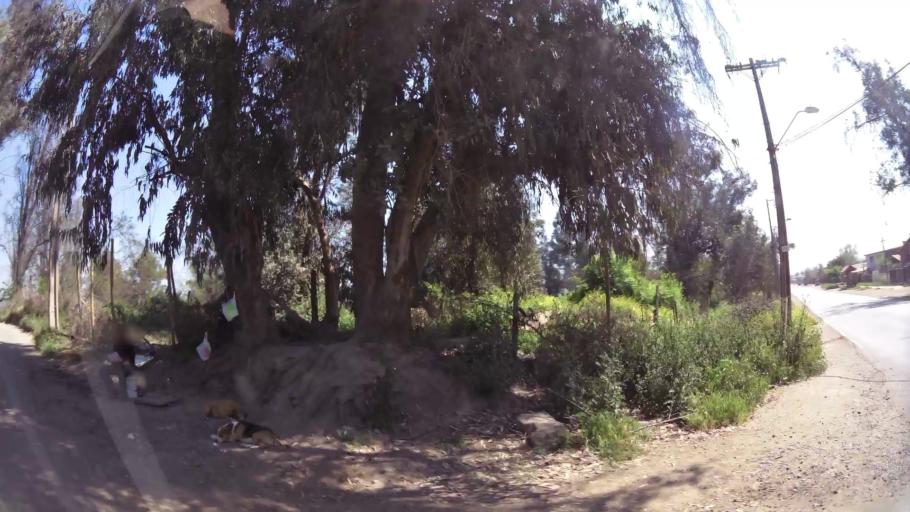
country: CL
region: Santiago Metropolitan
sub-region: Provincia de Talagante
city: Penaflor
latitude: -33.5890
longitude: -70.8062
